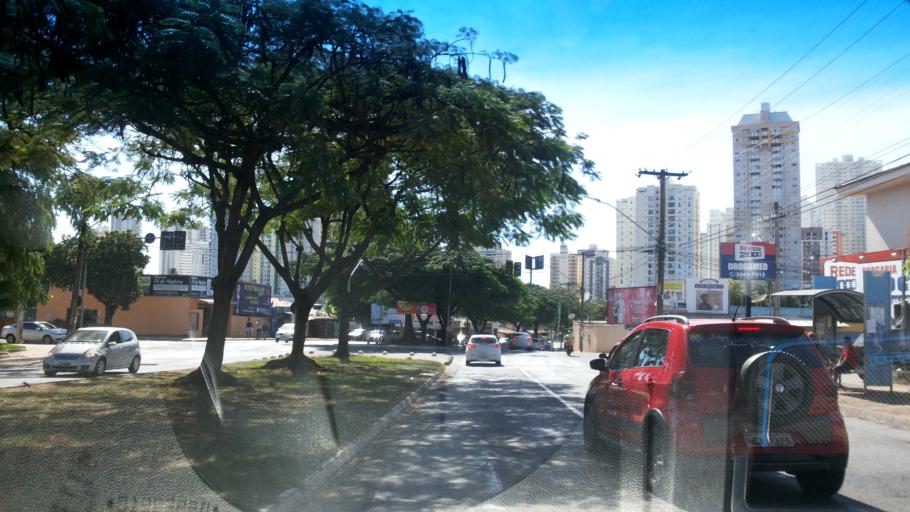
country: BR
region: Goias
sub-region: Goiania
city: Goiania
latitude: -16.7030
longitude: -49.2458
